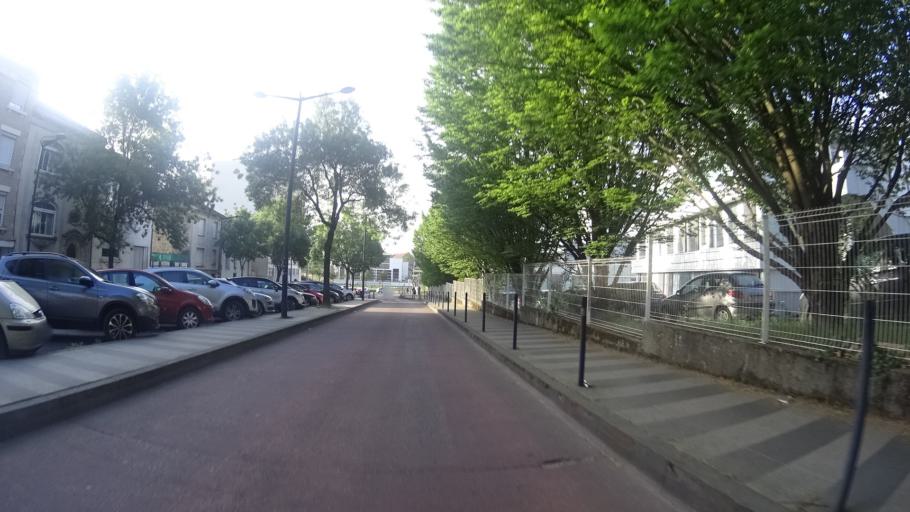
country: FR
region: Aquitaine
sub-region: Departement de la Gironde
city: Talence
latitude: 44.8280
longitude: -0.6024
